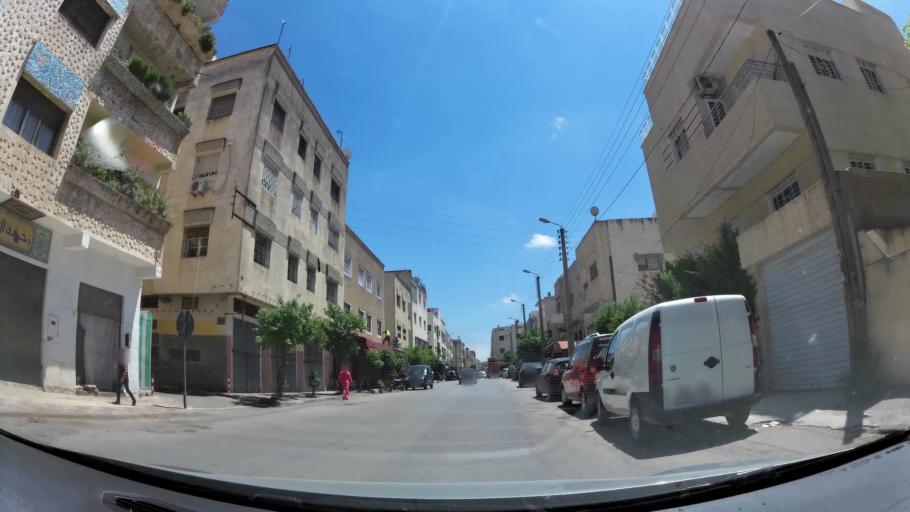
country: MA
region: Fes-Boulemane
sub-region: Fes
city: Fes
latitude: 34.0155
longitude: -4.9906
